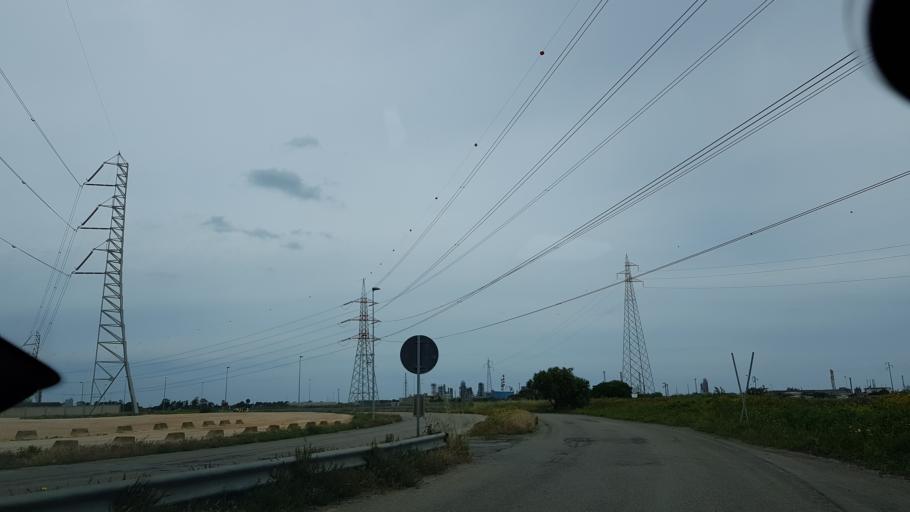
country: IT
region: Apulia
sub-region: Provincia di Brindisi
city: La Rosa
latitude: 40.6243
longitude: 17.9815
